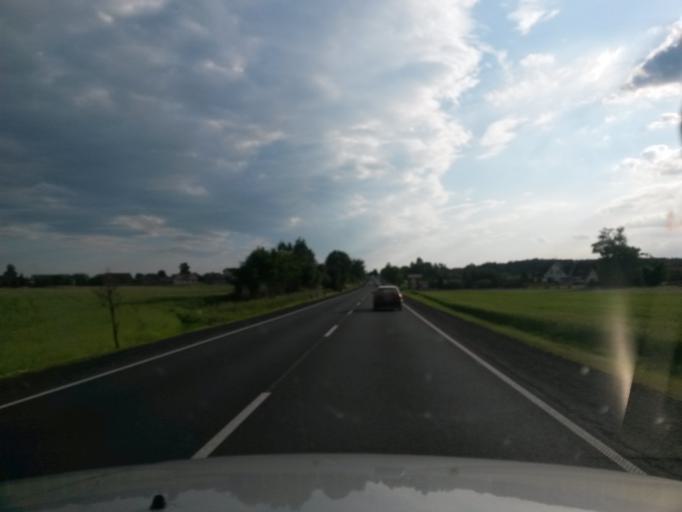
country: PL
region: Lodz Voivodeship
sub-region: Powiat piotrkowski
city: Grabica
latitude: 51.4161
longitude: 19.4743
